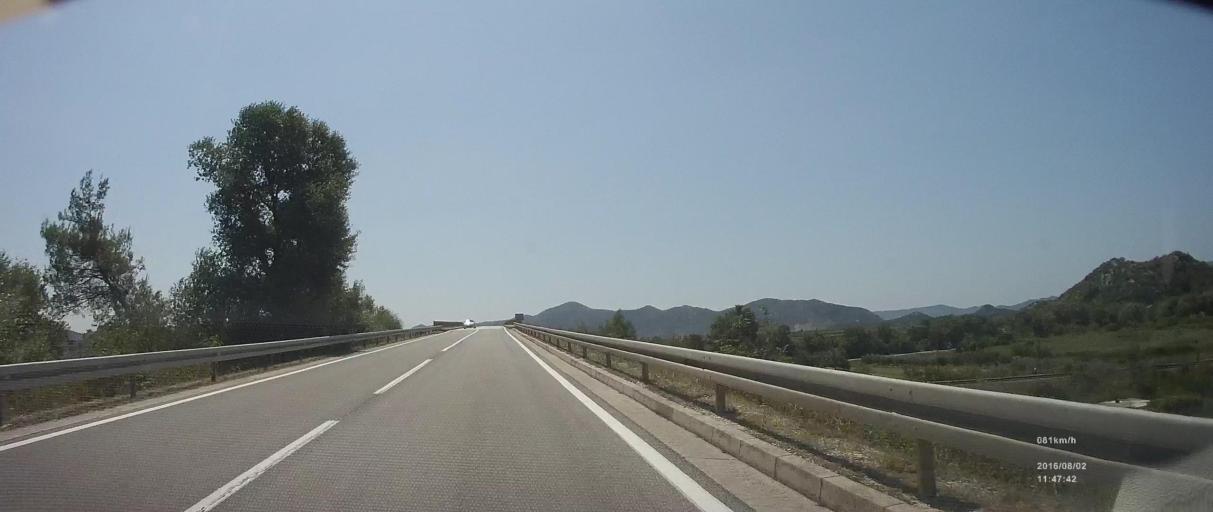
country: HR
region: Dubrovacko-Neretvanska
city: Komin
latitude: 43.0410
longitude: 17.4836
